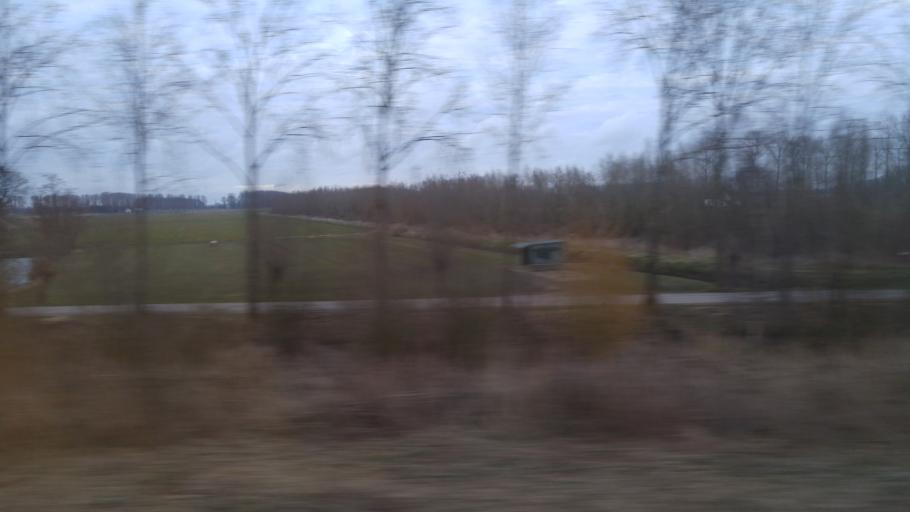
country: NL
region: Gelderland
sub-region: Gemeente Culemborg
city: Culemborg
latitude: 51.9288
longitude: 5.2419
